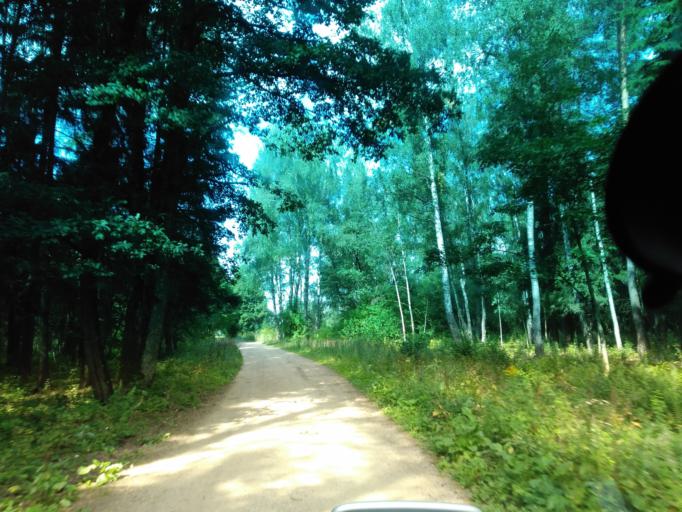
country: BY
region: Minsk
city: Stan'kava
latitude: 53.6228
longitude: 27.3158
